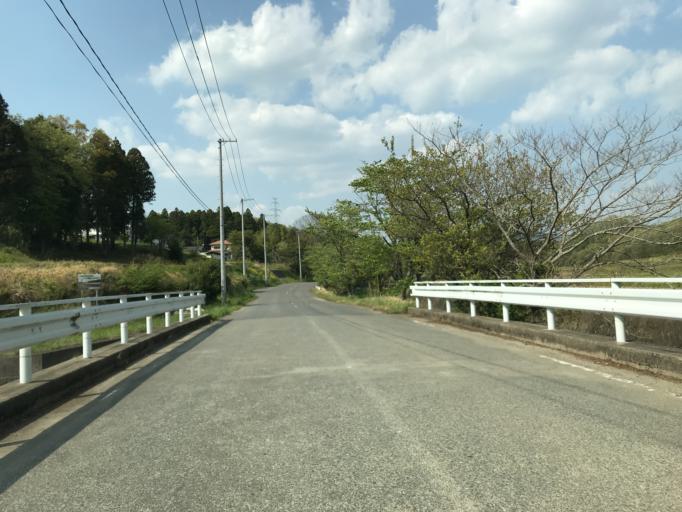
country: JP
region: Fukushima
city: Iwaki
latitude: 36.9613
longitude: 140.7543
